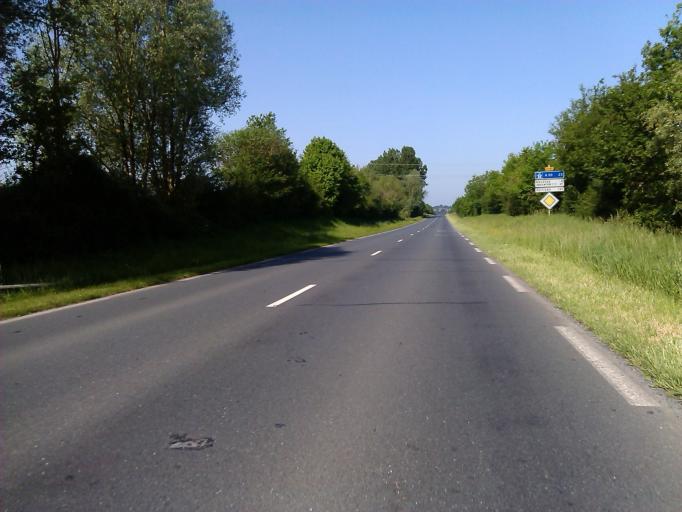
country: FR
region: Centre
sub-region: Departement de l'Indre
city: Neuvy-Saint-Sepulchre
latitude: 46.5990
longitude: 1.7643
